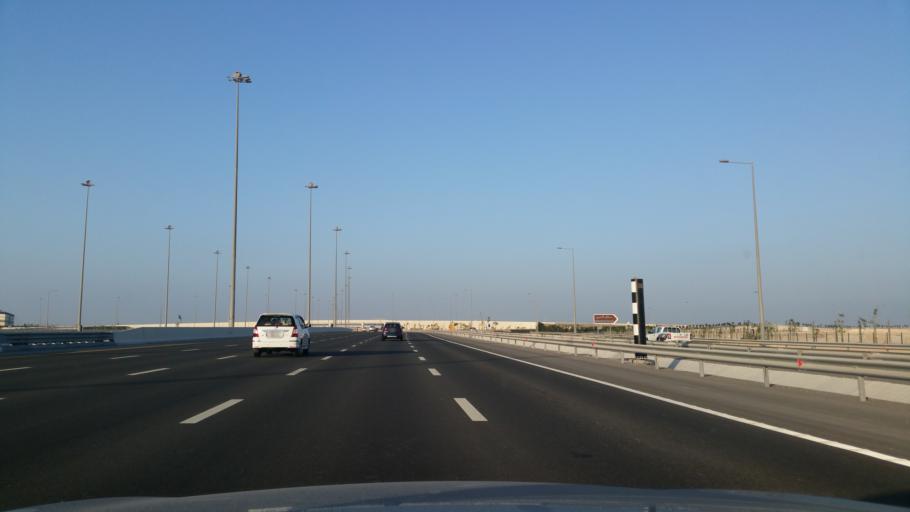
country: QA
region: Al Khawr
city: Al Khawr
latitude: 25.6341
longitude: 51.4903
